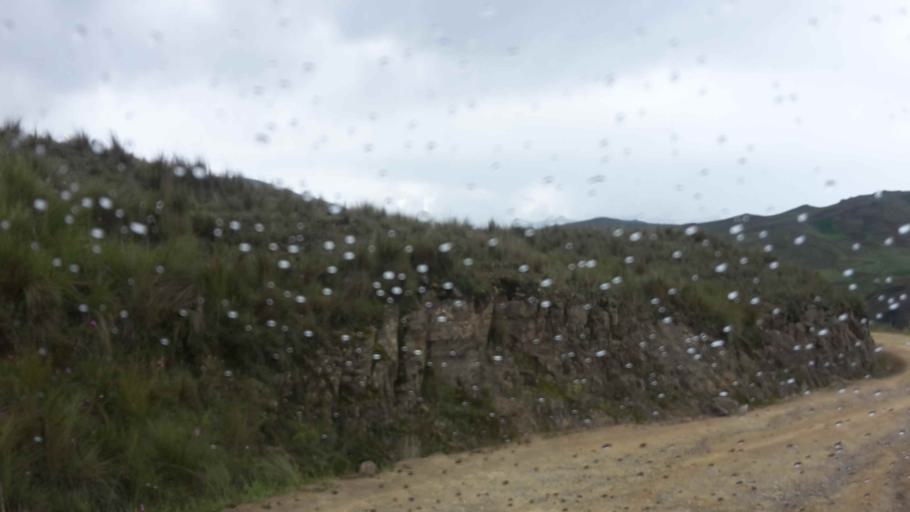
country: BO
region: Cochabamba
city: Cochabamba
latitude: -17.1432
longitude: -66.1036
